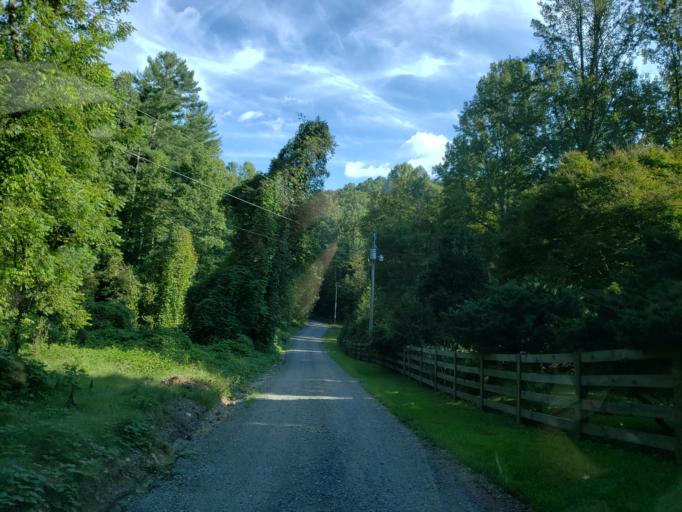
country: US
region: Georgia
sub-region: Fannin County
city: Blue Ridge
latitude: 34.6851
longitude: -84.2672
